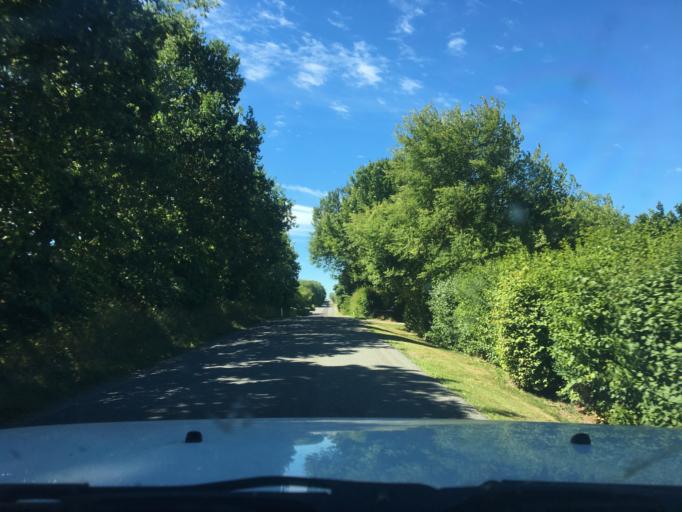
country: DK
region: Central Jutland
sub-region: Syddjurs Kommune
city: Hornslet
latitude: 56.3357
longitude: 10.3978
